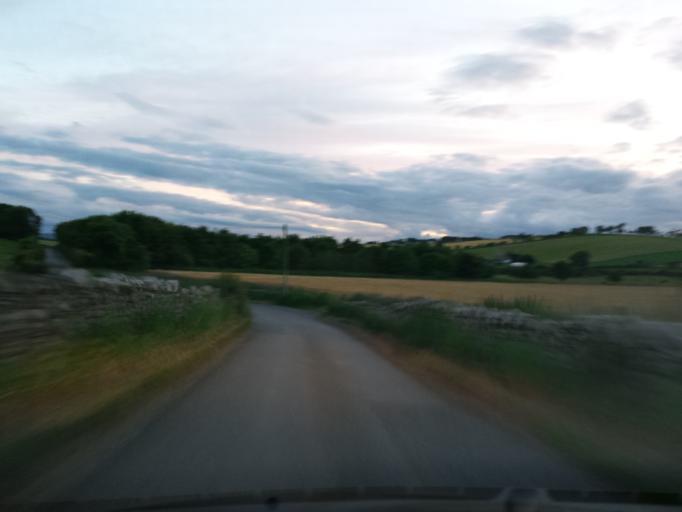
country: GB
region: Scotland
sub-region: The Scottish Borders
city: Chirnside
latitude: 55.8416
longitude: -2.2406
